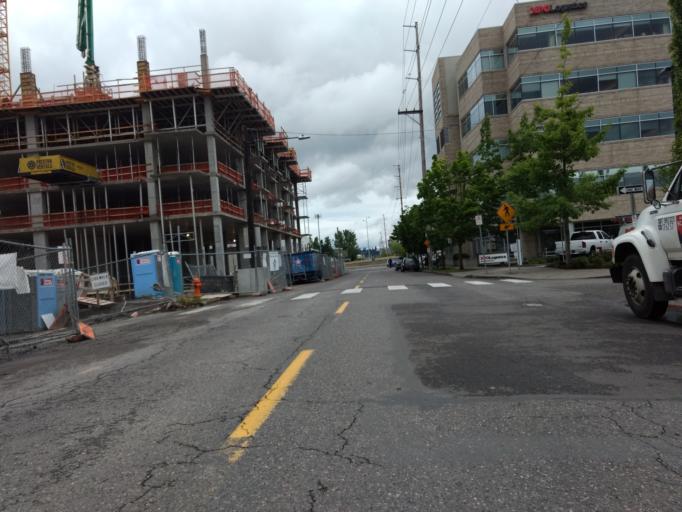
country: US
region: Oregon
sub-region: Multnomah County
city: Portland
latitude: 45.5347
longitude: -122.6947
